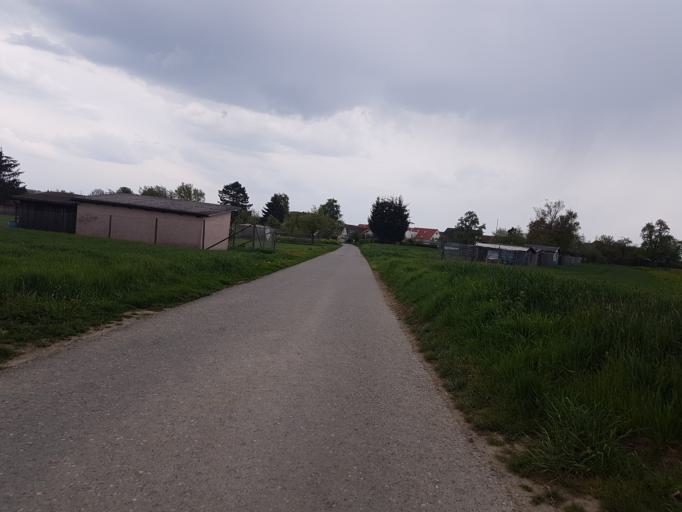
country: DE
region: Baden-Wuerttemberg
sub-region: Regierungsbezirk Stuttgart
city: Bondorf
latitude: 48.4990
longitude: 8.8060
